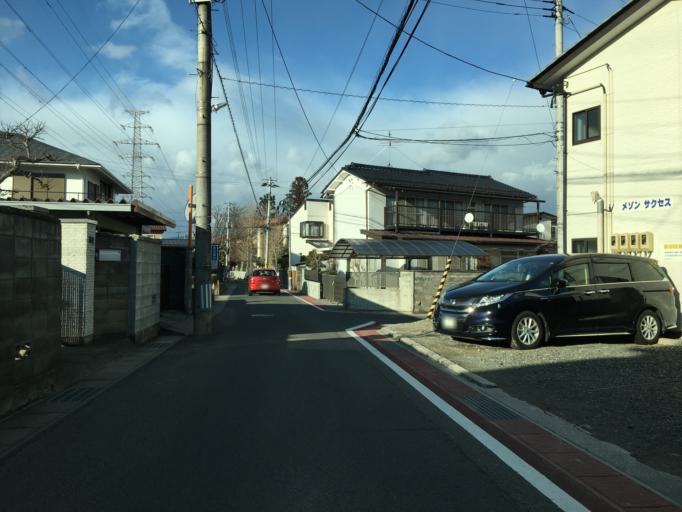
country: JP
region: Fukushima
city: Fukushima-shi
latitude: 37.7783
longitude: 140.4420
